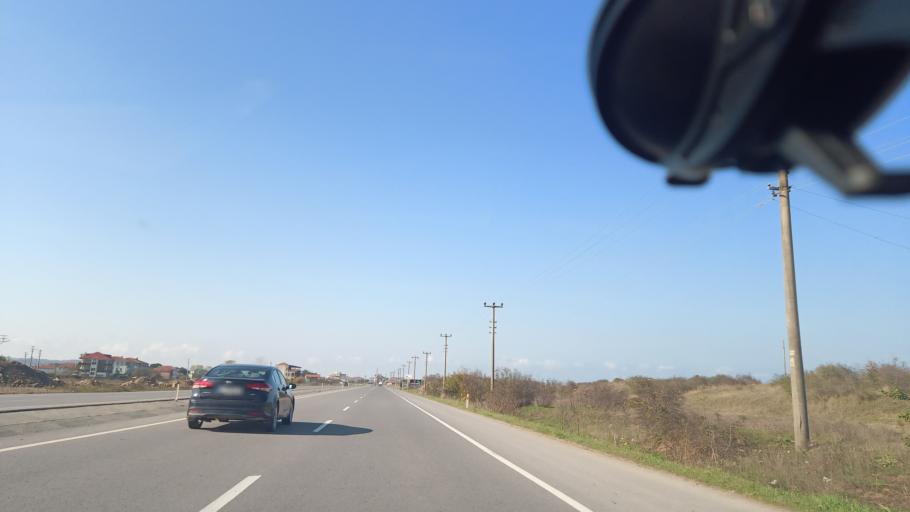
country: TR
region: Sakarya
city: Karasu
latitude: 41.0845
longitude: 30.7572
